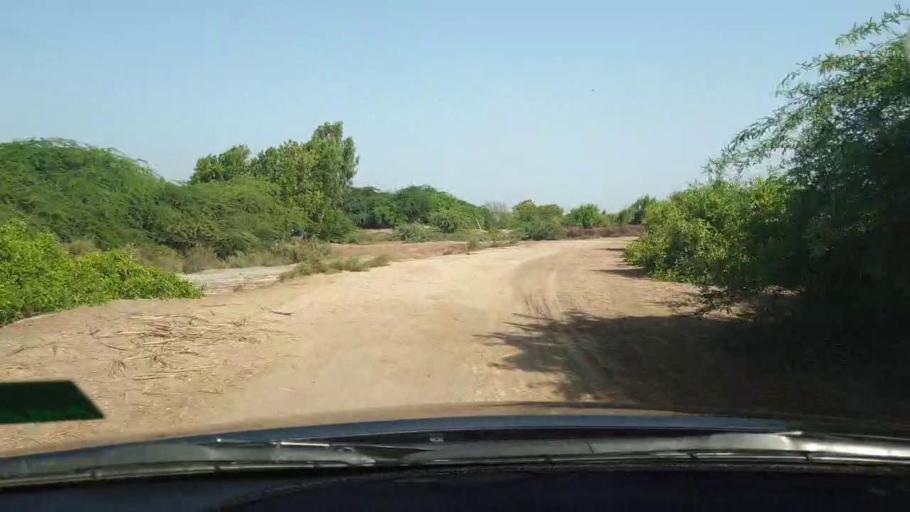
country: PK
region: Sindh
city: Tando Bago
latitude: 24.7184
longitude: 68.9909
